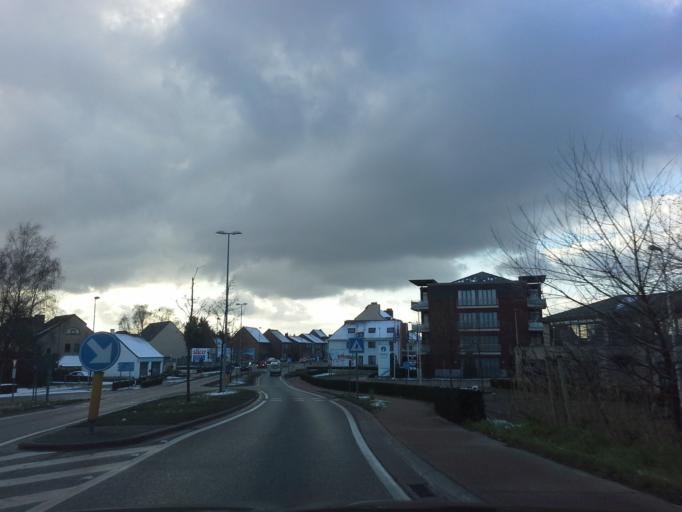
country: BE
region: Flanders
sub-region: Provincie Limburg
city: Neerpelt
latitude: 51.2313
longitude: 5.4438
